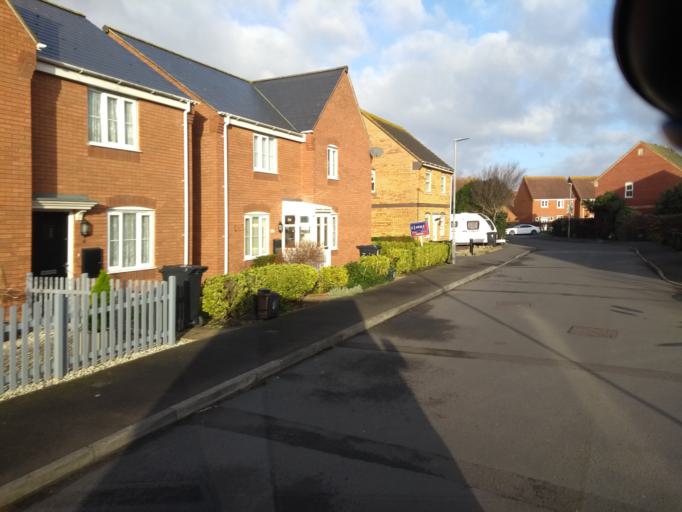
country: GB
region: England
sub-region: Somerset
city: Highbridge
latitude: 51.2316
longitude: -2.9803
